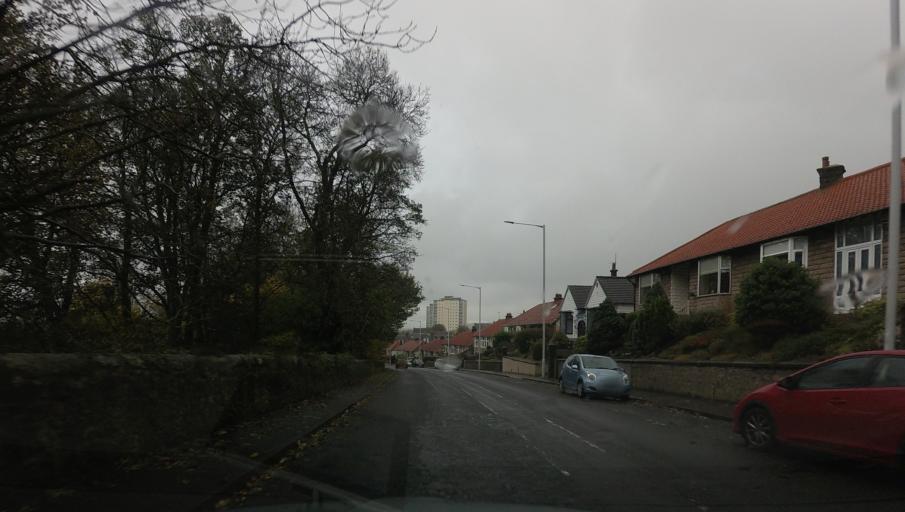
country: GB
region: Scotland
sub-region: Fife
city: Kirkcaldy
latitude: 56.1227
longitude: -3.1360
